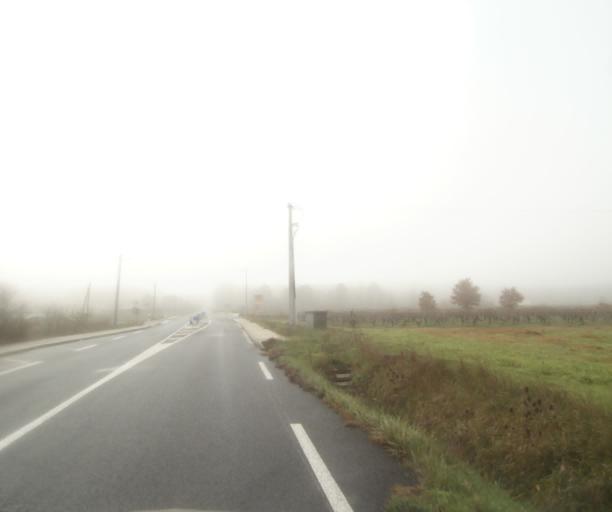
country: FR
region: Midi-Pyrenees
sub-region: Departement de la Haute-Garonne
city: Villaudric
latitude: 43.8255
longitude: 1.4716
